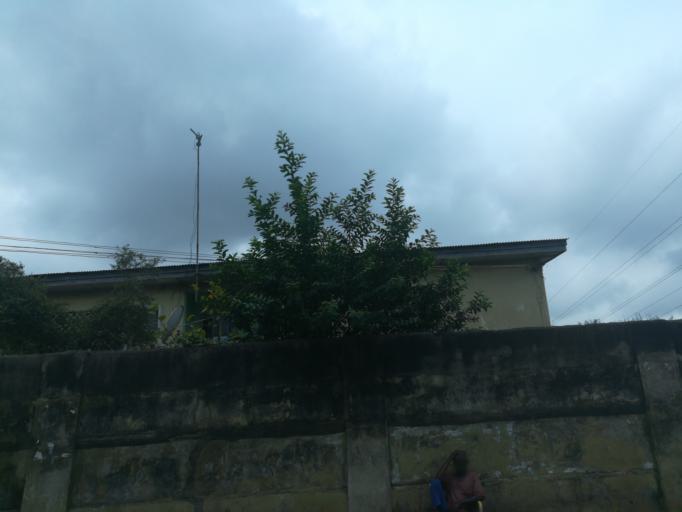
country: NG
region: Lagos
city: Ojota
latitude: 6.5696
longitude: 3.3654
